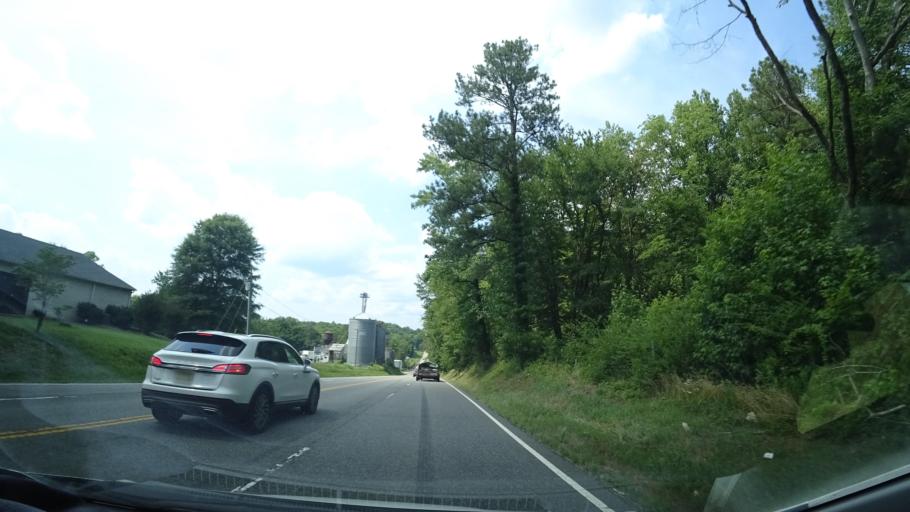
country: US
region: Virginia
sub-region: Hanover County
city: Ashland
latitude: 37.8047
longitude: -77.4727
